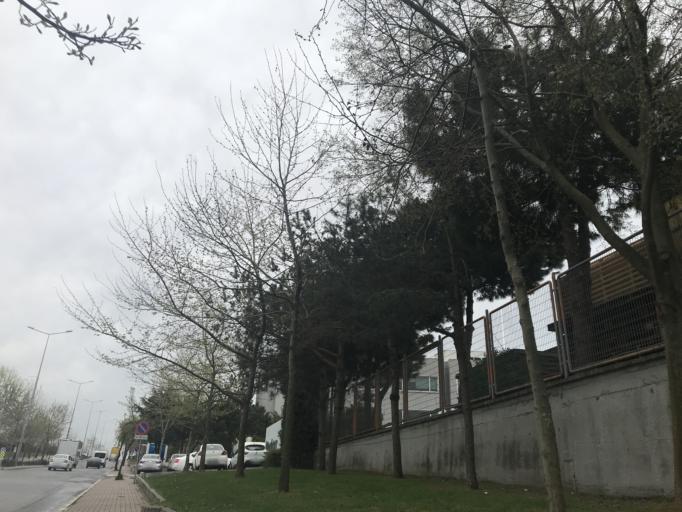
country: TR
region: Istanbul
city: Umraniye
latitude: 41.0032
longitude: 29.1707
